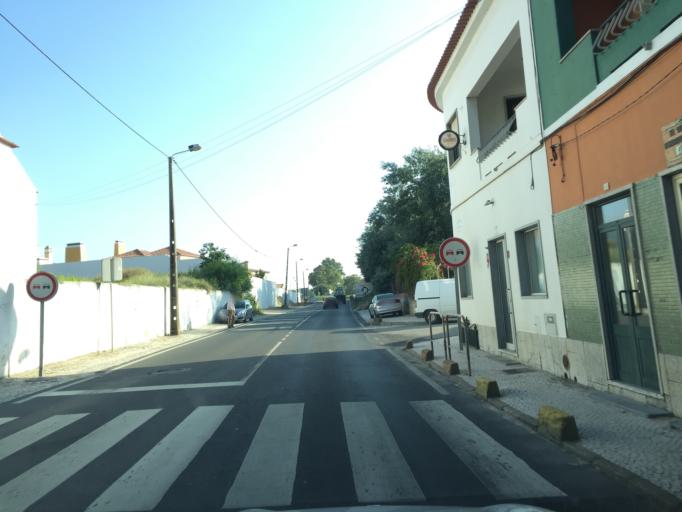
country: PT
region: Santarem
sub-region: Almeirim
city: Almeirim
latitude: 39.2060
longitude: -8.6341
